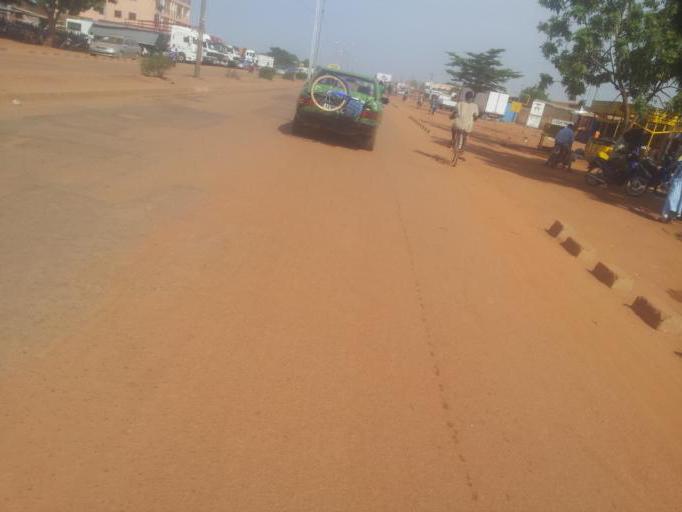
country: BF
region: Centre
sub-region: Kadiogo Province
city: Ouagadougou
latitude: 12.3893
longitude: -1.5742
